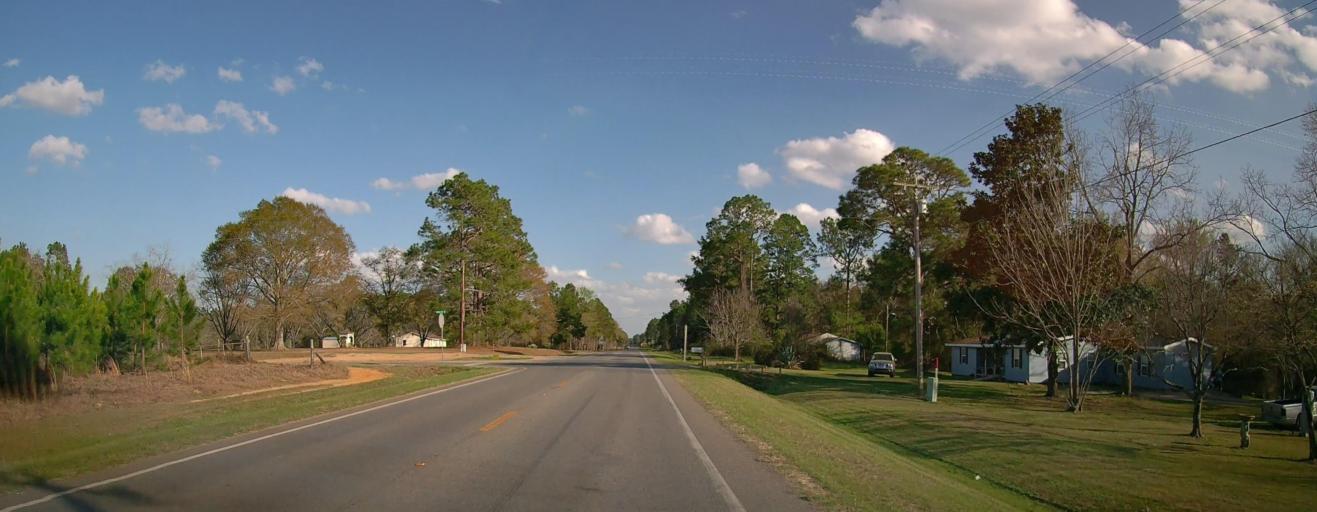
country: US
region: Georgia
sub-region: Toombs County
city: Lyons
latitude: 32.1849
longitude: -82.2983
